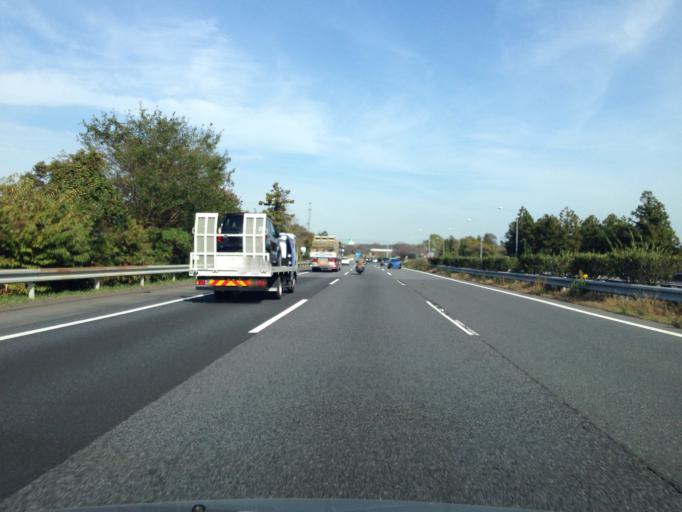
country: JP
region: Ibaraki
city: Ishioka
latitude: 36.1425
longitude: 140.2077
